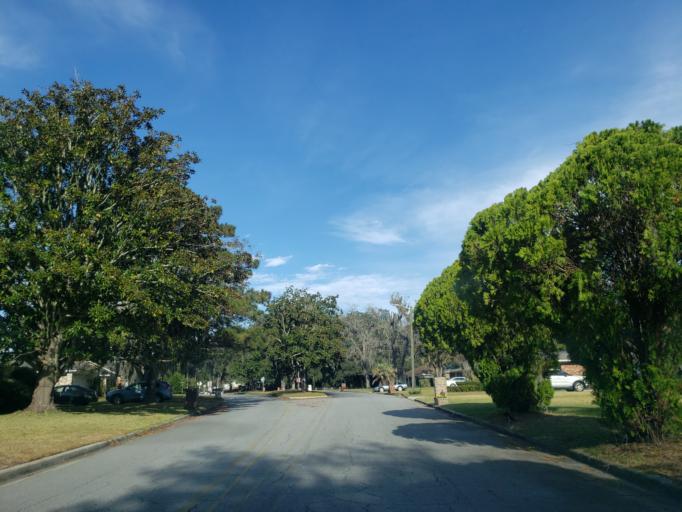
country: US
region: Georgia
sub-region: Chatham County
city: Isle of Hope
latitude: 31.9896
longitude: -81.0927
